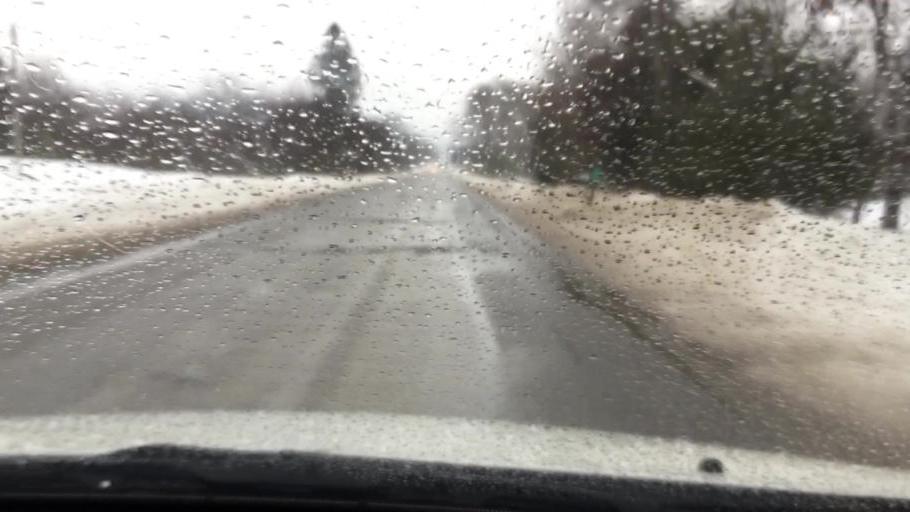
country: US
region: Michigan
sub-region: Charlevoix County
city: East Jordan
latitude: 45.1326
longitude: -85.1455
